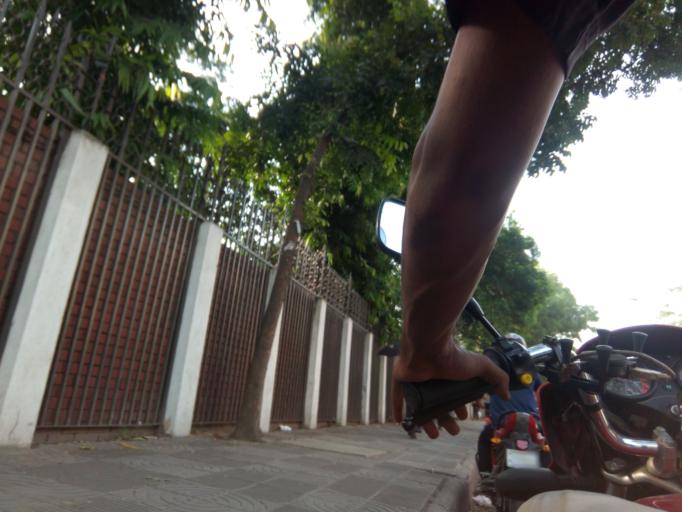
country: BD
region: Dhaka
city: Paltan
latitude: 23.7387
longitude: 90.4054
